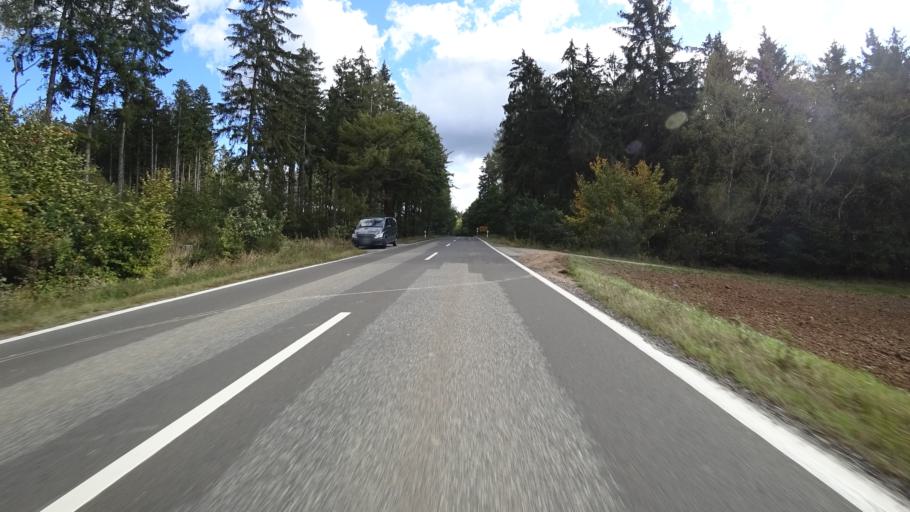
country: DE
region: Rheinland-Pfalz
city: Morschbach
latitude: 50.0090
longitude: 7.6351
